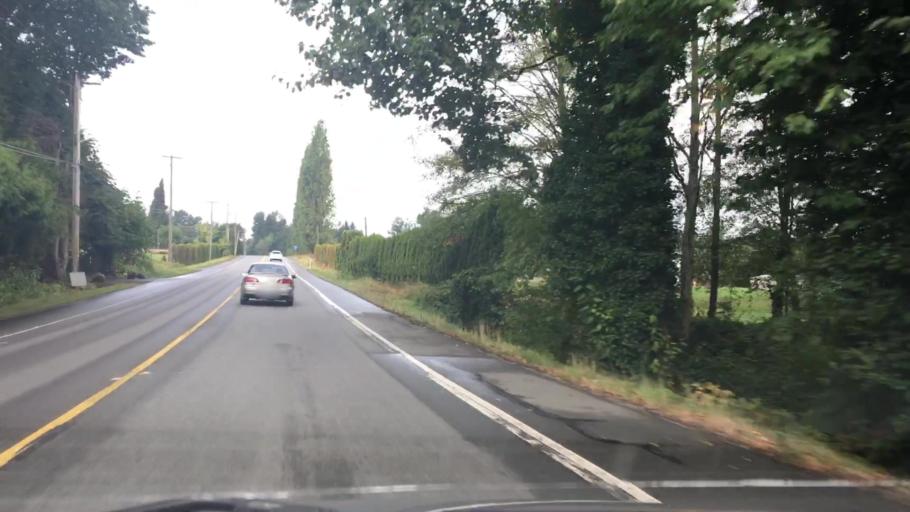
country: CA
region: British Columbia
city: Langley
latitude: 49.1045
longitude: -122.5989
